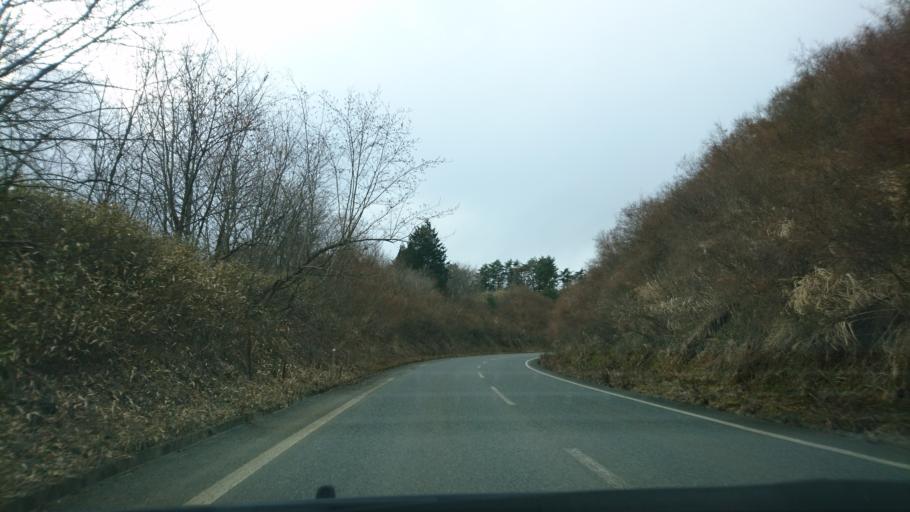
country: JP
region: Iwate
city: Ichinoseki
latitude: 38.8518
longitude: 141.2078
